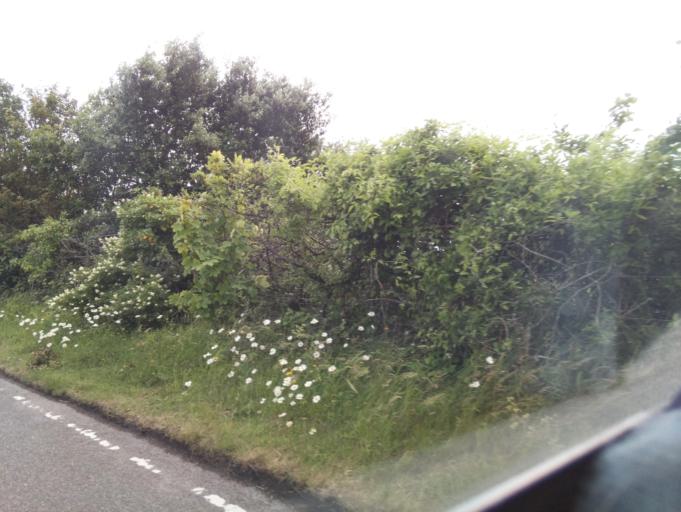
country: GB
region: Wales
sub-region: Vale of Glamorgan
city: Rhoose
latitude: 51.3891
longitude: -3.3866
